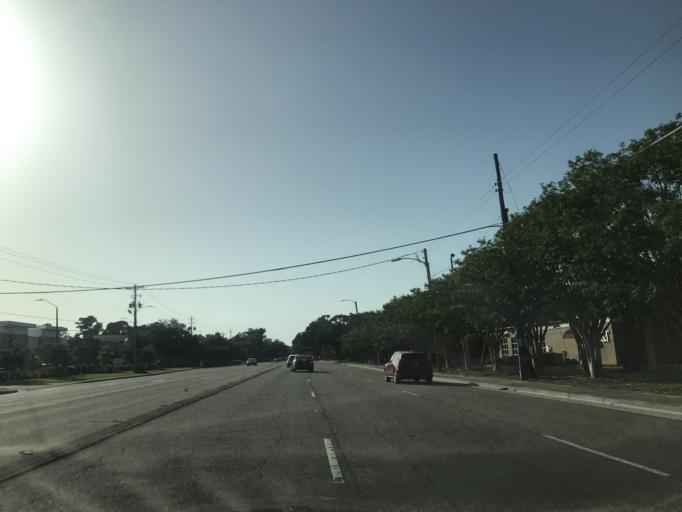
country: US
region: North Carolina
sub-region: New Hanover County
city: Wilmington
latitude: 34.2163
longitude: -77.9046
